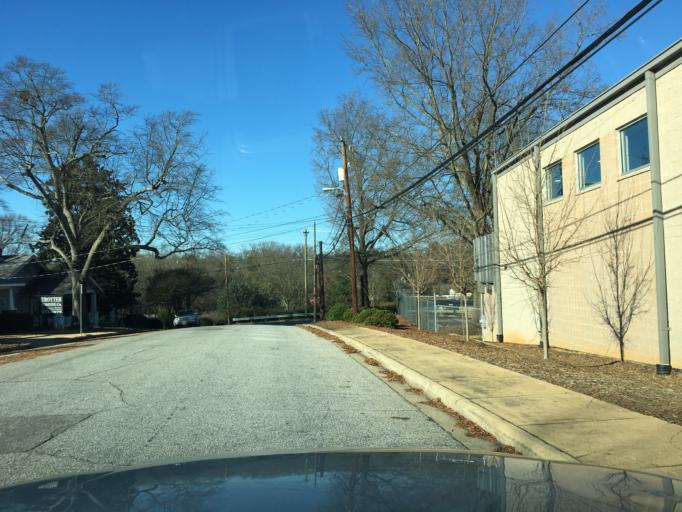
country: US
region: South Carolina
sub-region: Greenville County
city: Greenville
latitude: 34.8542
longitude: -82.3888
